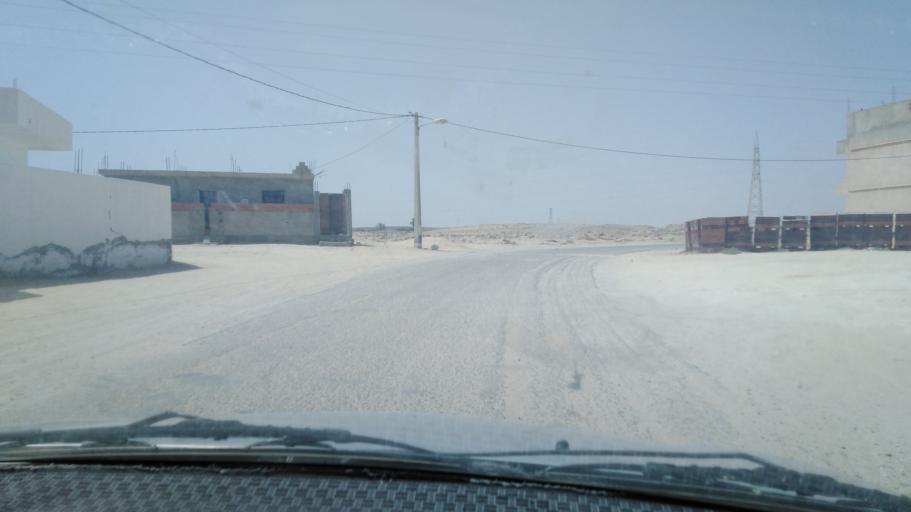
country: TN
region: Qabis
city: Gabes
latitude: 33.9541
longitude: 9.9937
